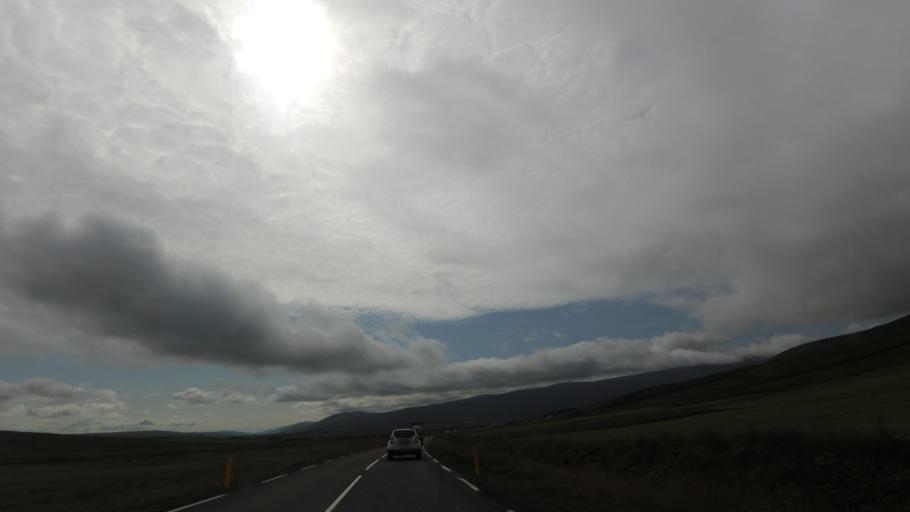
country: IS
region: Northeast
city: Laugar
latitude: 65.7347
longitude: -17.5908
